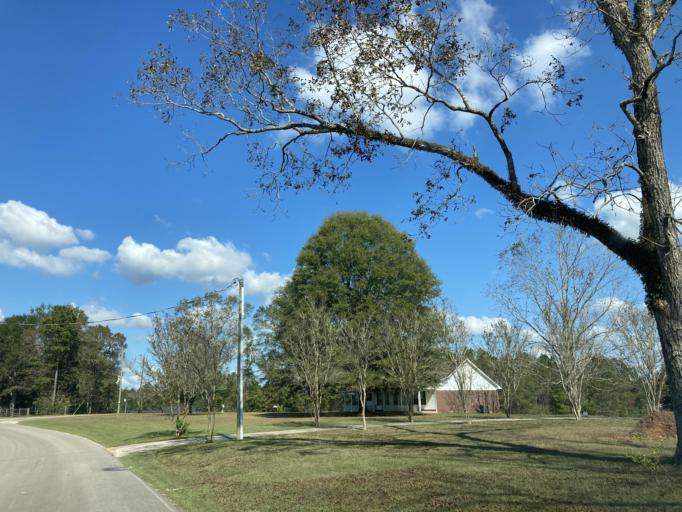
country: US
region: Mississippi
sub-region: Lamar County
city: Sumrall
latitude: 31.3347
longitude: -89.5399
